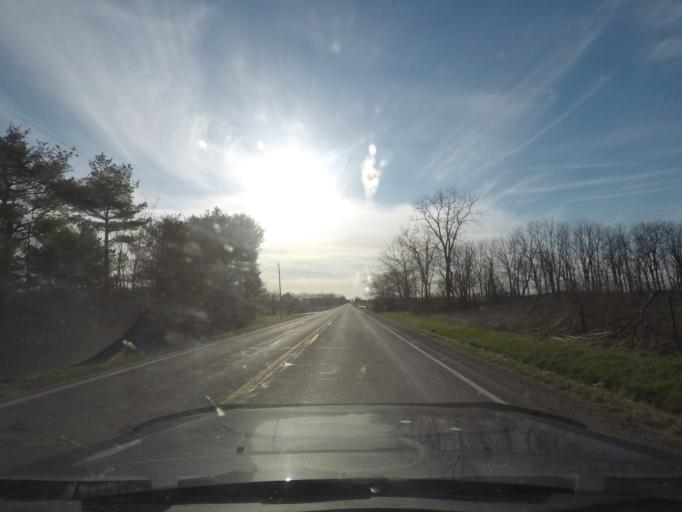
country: US
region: Indiana
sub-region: Saint Joseph County
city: Walkerton
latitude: 41.4483
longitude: -86.3957
